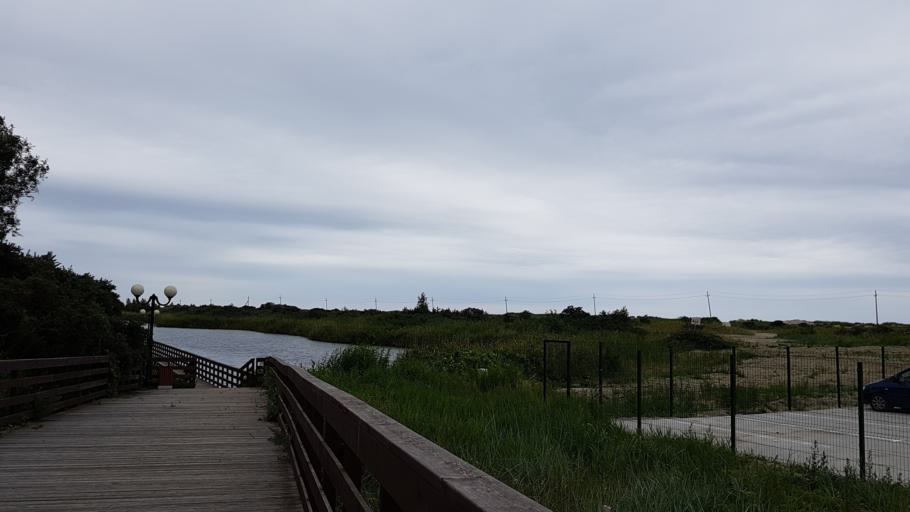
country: RU
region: Kaliningrad
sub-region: Gorod Kaliningrad
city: Yantarnyy
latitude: 54.8829
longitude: 19.9342
